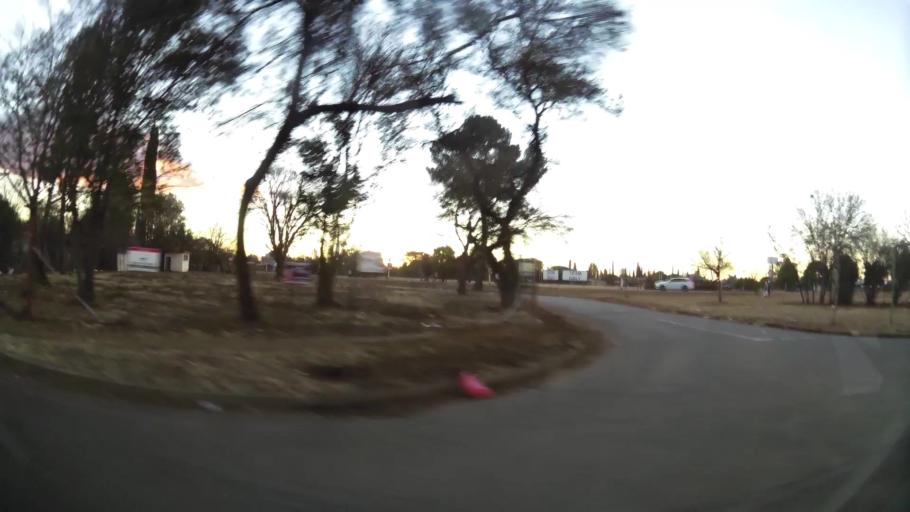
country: ZA
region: North-West
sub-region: Dr Kenneth Kaunda District Municipality
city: Potchefstroom
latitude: -26.7091
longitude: 27.1166
